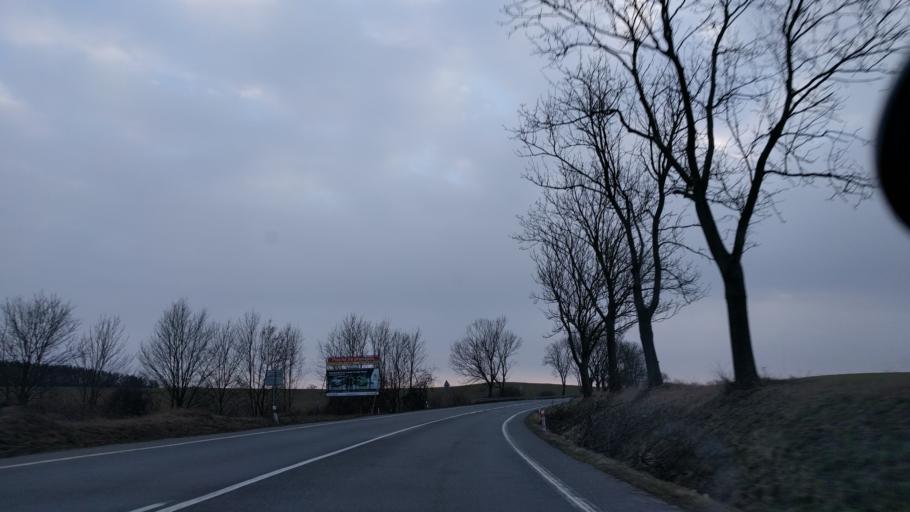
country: CZ
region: Jihocesky
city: Radomysl
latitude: 49.2781
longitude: 13.9465
